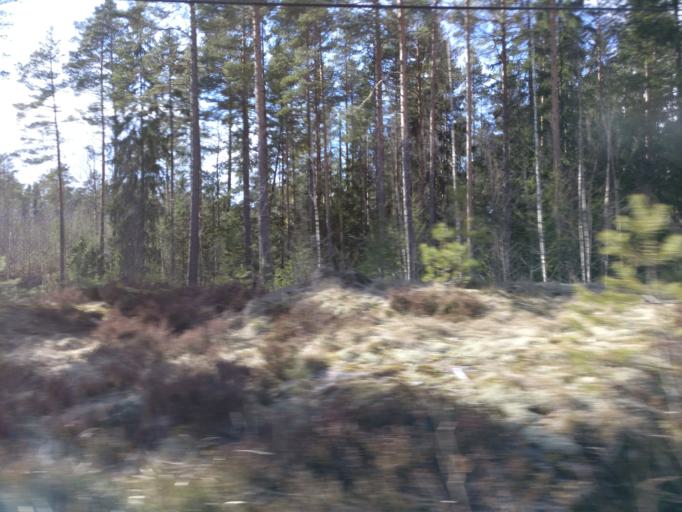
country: FI
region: Varsinais-Suomi
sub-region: Salo
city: Suomusjaervi
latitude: 60.3453
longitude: 23.6463
